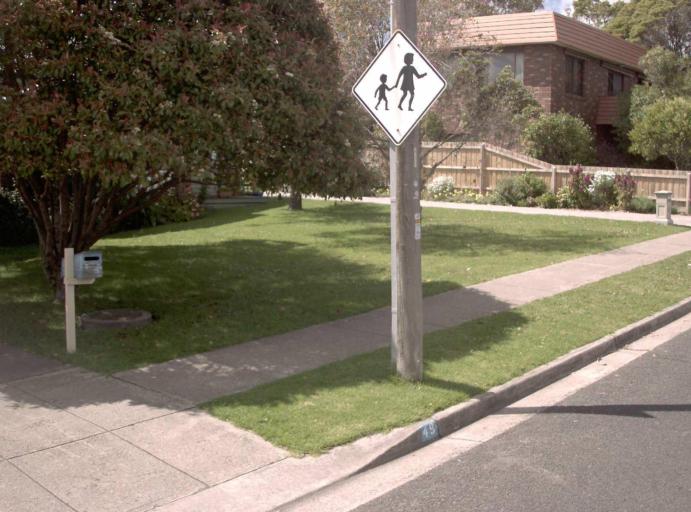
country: AU
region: Victoria
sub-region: Mornington Peninsula
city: Dromana
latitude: -38.3391
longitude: 144.9606
